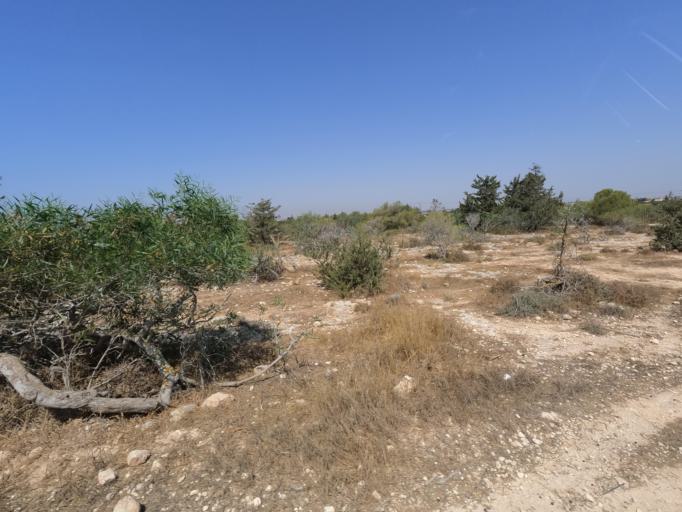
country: CY
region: Ammochostos
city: Paralimni
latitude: 35.0116
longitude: 33.9676
